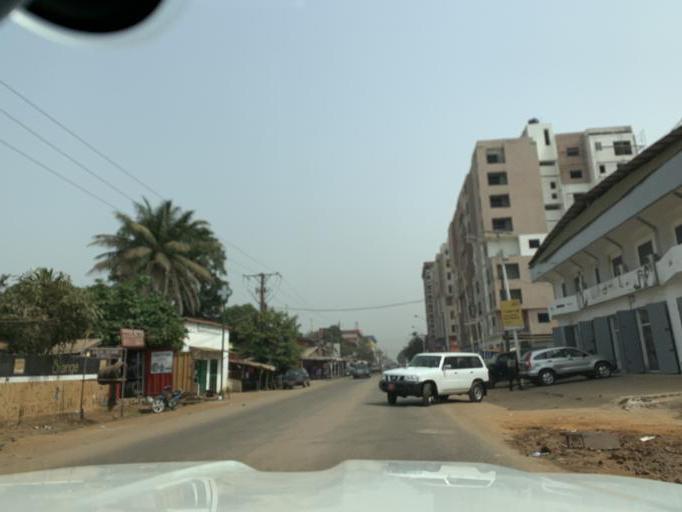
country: GN
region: Conakry
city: Camayenne
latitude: 9.5258
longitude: -13.6853
